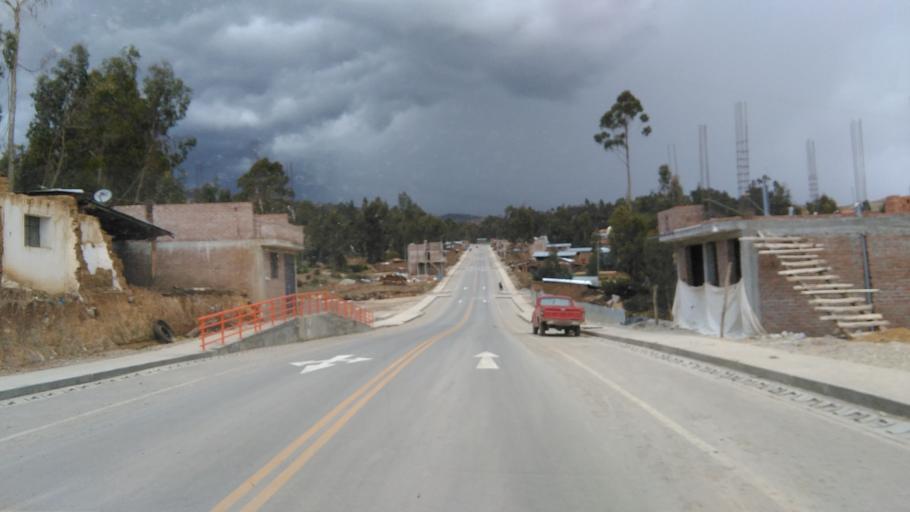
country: PE
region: Apurimac
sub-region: Provincia de Andahuaylas
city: San Jeronimo
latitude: -13.7305
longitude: -73.3517
